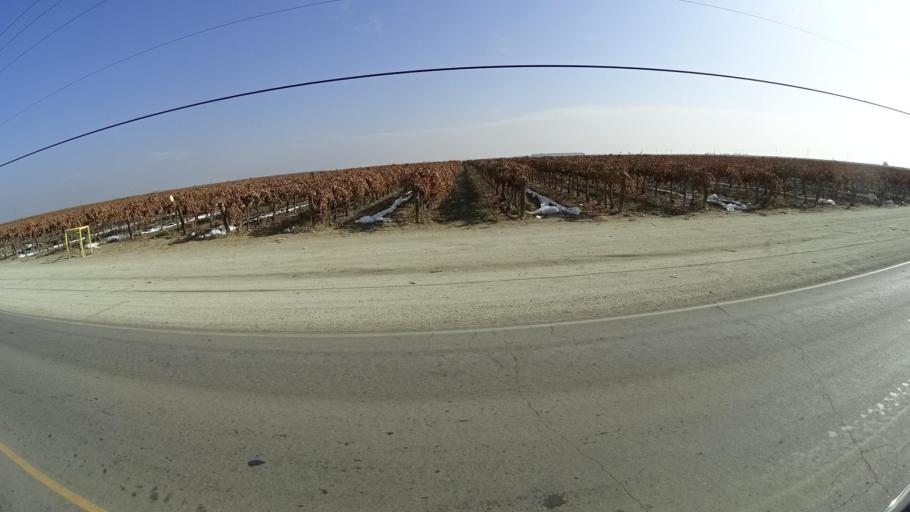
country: US
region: California
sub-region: Kern County
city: McFarland
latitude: 35.7073
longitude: -119.2231
